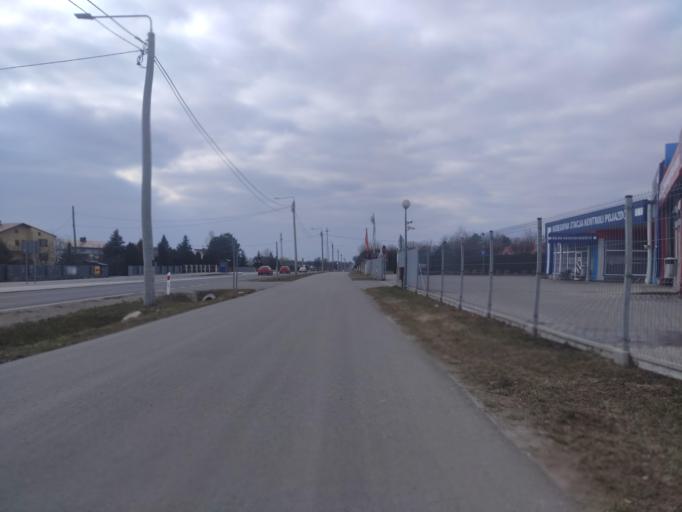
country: PL
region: Lublin Voivodeship
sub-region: Powiat lubartowski
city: Kock
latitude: 51.6439
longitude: 22.4358
